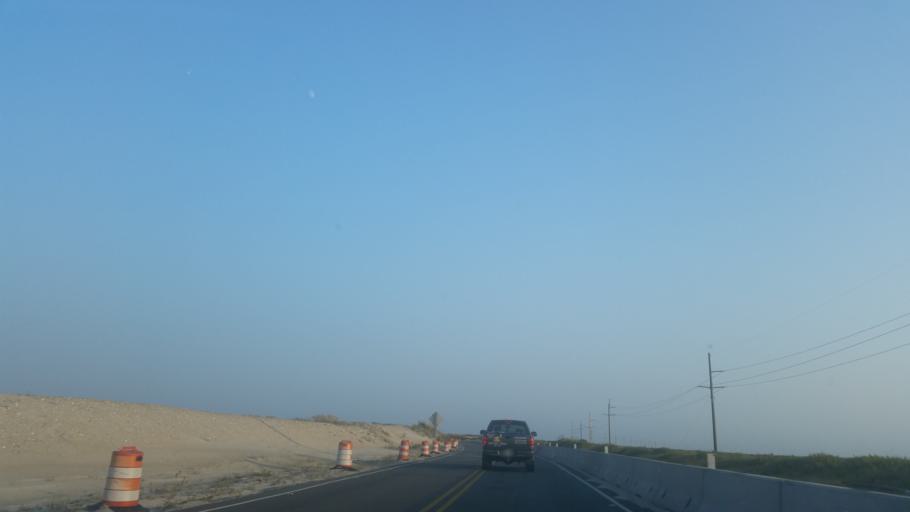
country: US
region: North Carolina
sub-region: Dare County
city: Wanchese
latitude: 35.6823
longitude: -75.4833
